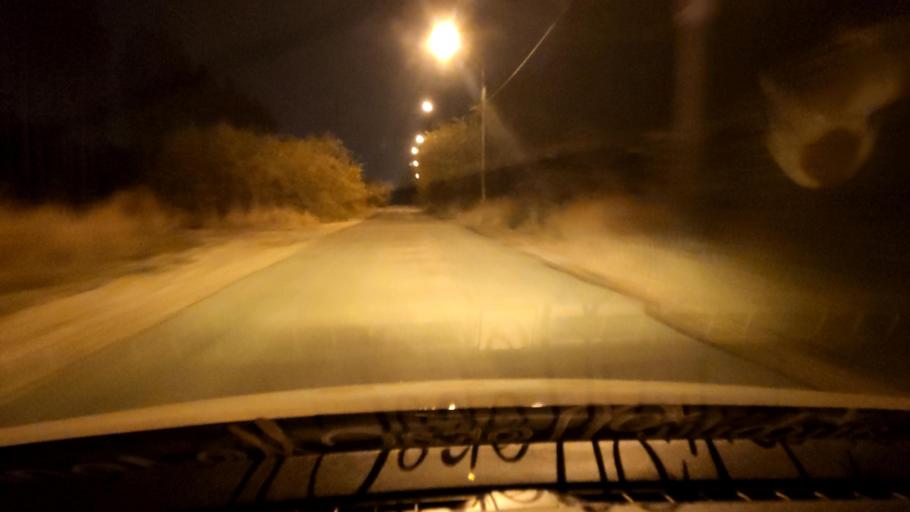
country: RU
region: Voronezj
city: Pridonskoy
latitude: 51.6843
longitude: 39.0941
